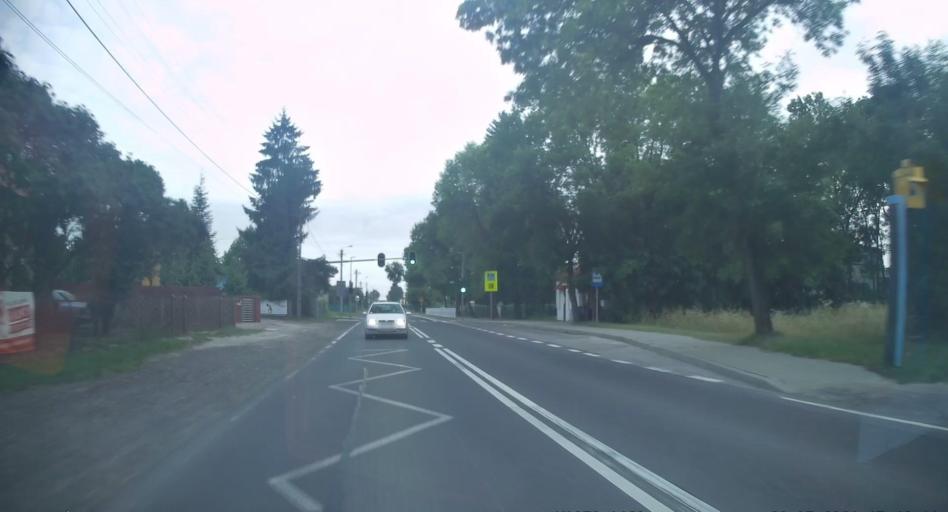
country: PL
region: Lodz Voivodeship
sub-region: Powiat radomszczanski
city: Radomsko
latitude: 51.0972
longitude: 19.4602
